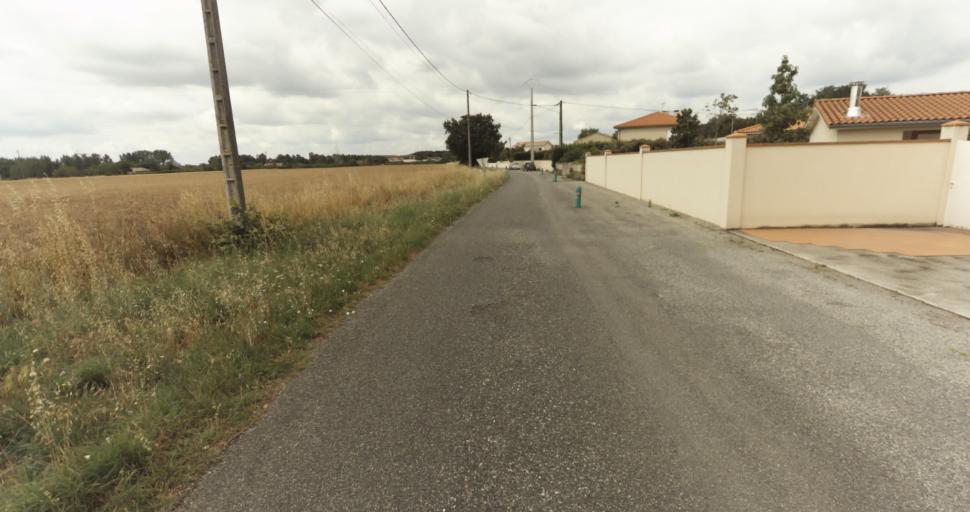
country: FR
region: Midi-Pyrenees
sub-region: Departement de la Haute-Garonne
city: Fonsorbes
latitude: 43.5490
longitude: 1.2179
